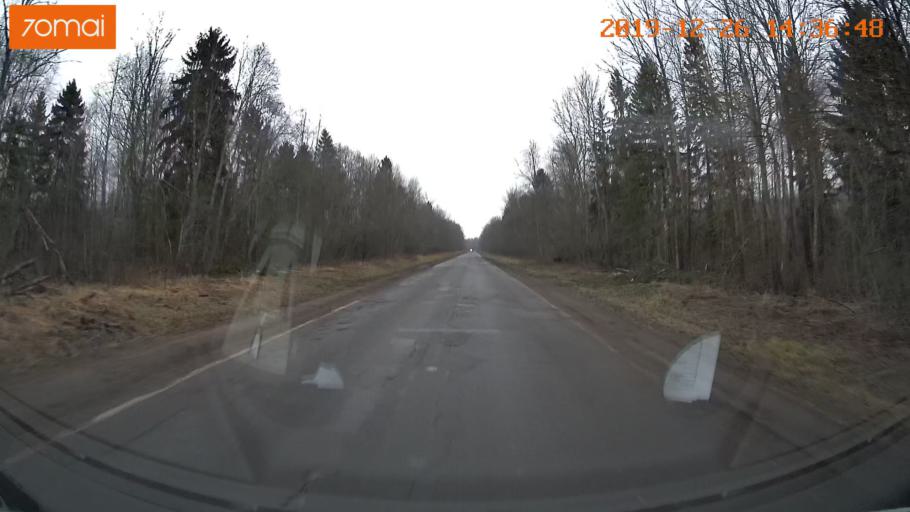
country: RU
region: Jaroslavl
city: Poshekhon'ye
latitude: 58.4081
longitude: 38.9747
